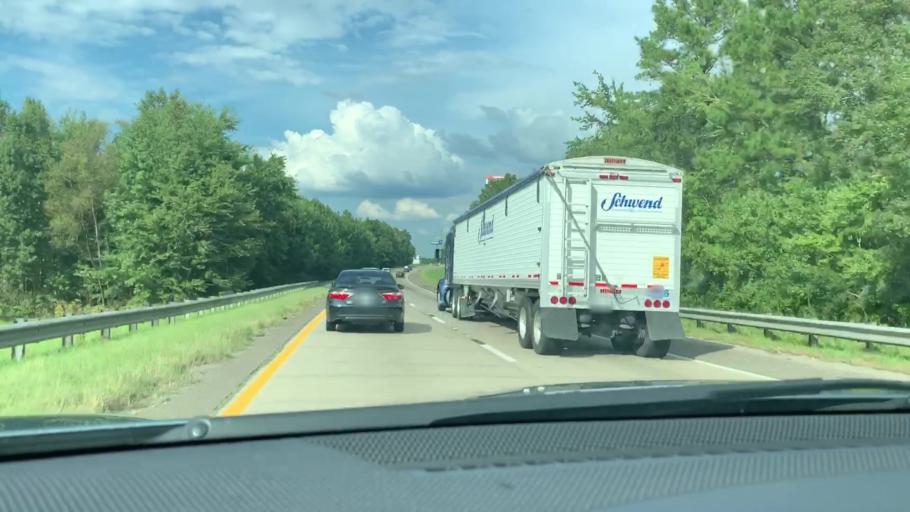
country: US
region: South Carolina
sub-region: Hampton County
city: Yemassee
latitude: 32.6896
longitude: -80.8803
